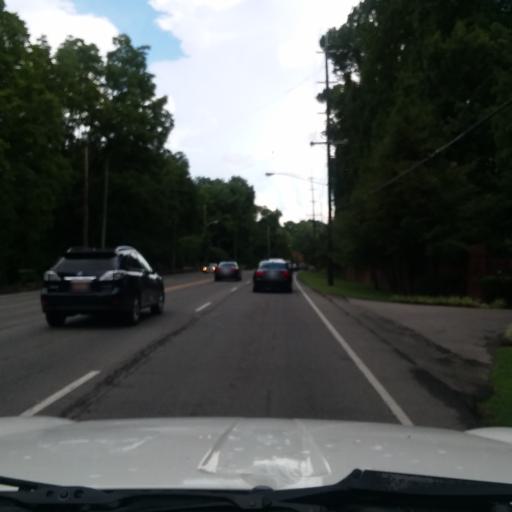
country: US
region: Tennessee
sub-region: Davidson County
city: Oak Hill
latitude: 36.0929
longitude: -86.7716
